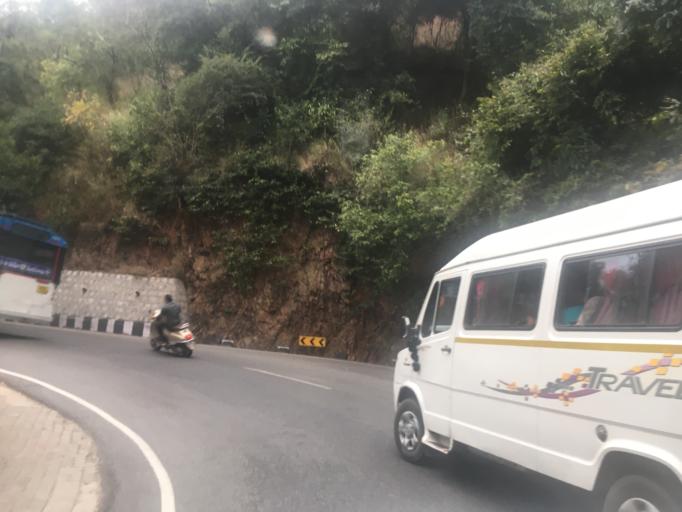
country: IN
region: Andhra Pradesh
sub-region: Chittoor
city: Tirumala
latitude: 13.6637
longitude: 79.3515
